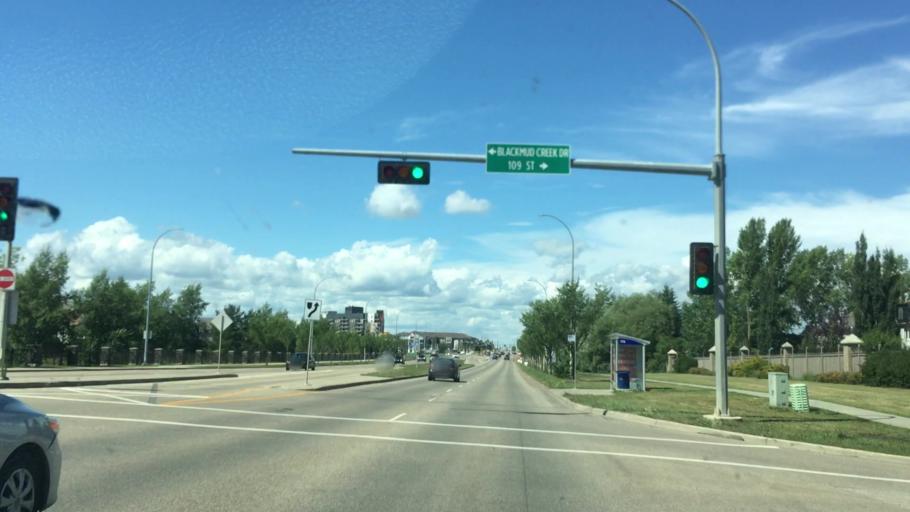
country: CA
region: Alberta
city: Beaumont
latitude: 53.4249
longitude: -113.5091
